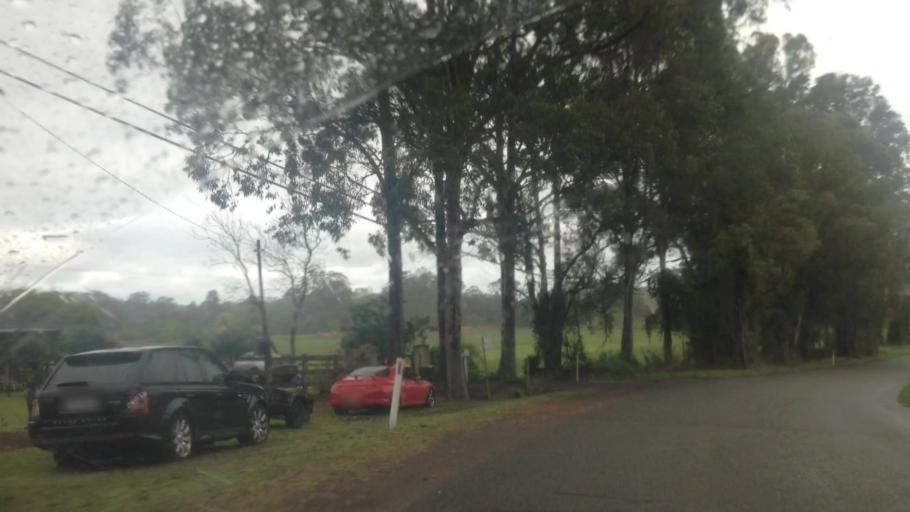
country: AU
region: New South Wales
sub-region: Wyong Shire
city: Little Jilliby
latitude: -33.2141
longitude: 151.3718
